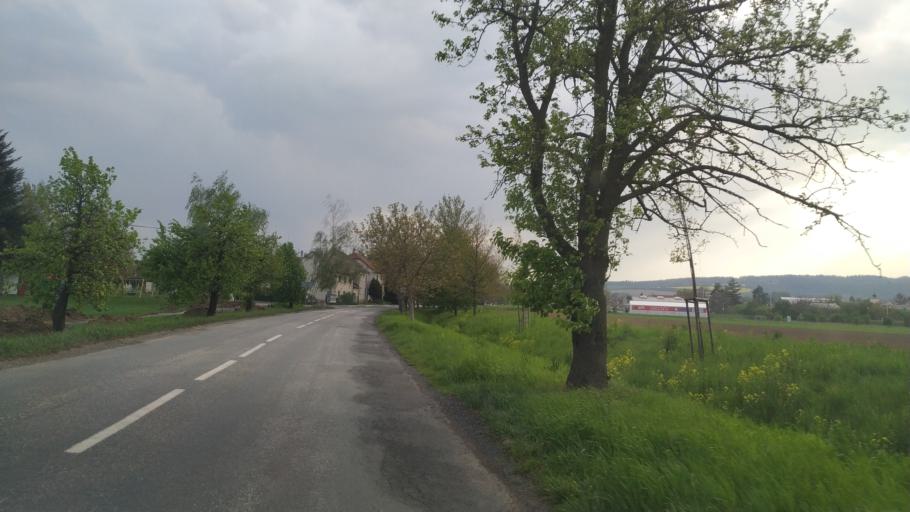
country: CZ
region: Olomoucky
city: Lutin
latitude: 49.5502
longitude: 17.1223
